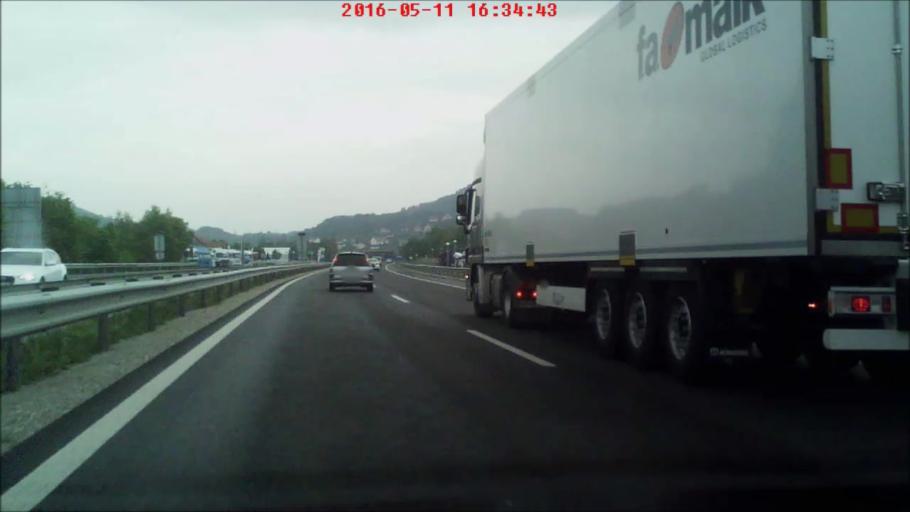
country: SI
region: Pesnica
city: Pesnica pri Mariboru
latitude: 46.6114
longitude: 15.6626
